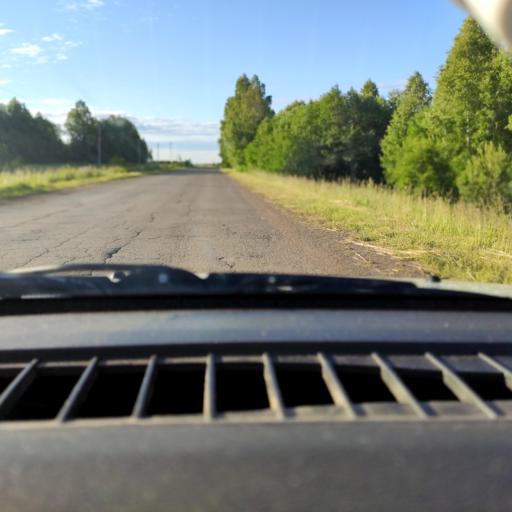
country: RU
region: Perm
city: Uinskoye
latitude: 57.0936
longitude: 56.5516
